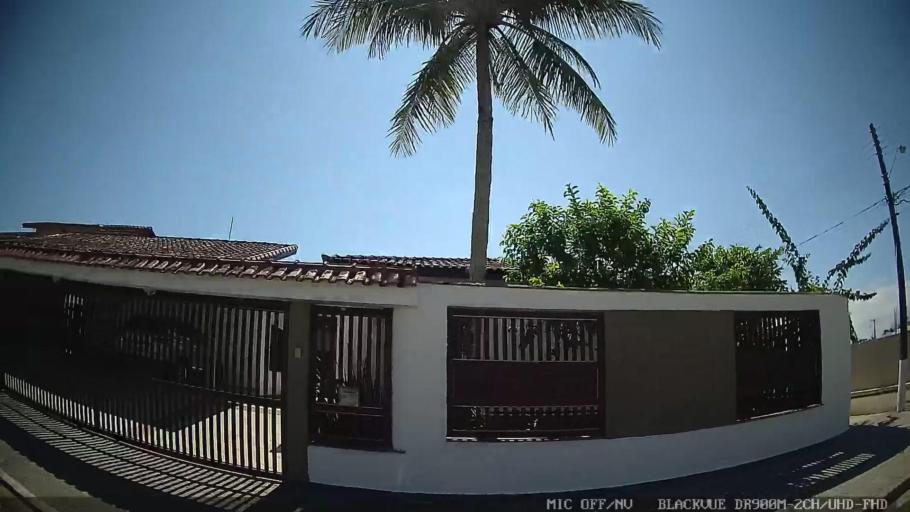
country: BR
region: Sao Paulo
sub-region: Peruibe
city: Peruibe
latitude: -24.3137
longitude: -46.9861
